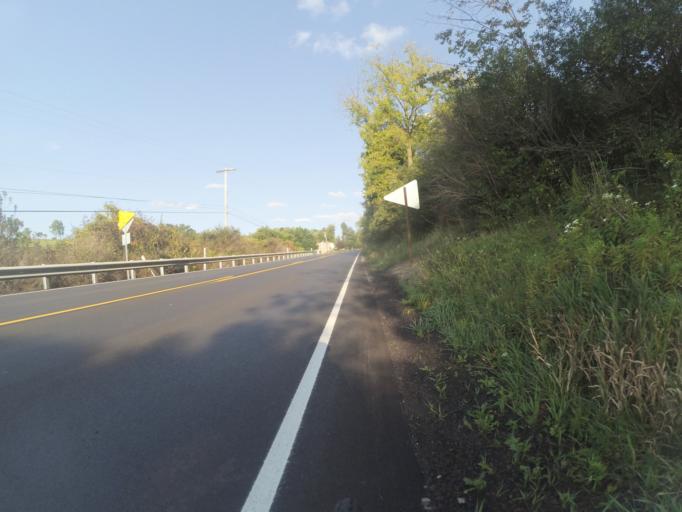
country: US
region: Pennsylvania
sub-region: Centre County
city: Boalsburg
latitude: 40.7918
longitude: -77.7448
